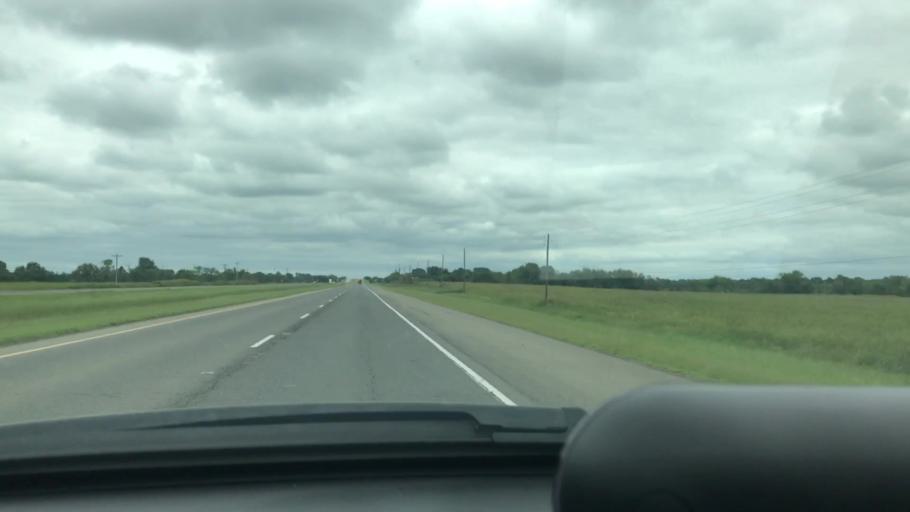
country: US
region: Oklahoma
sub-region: Wagoner County
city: Wagoner
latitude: 35.8596
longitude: -95.4025
